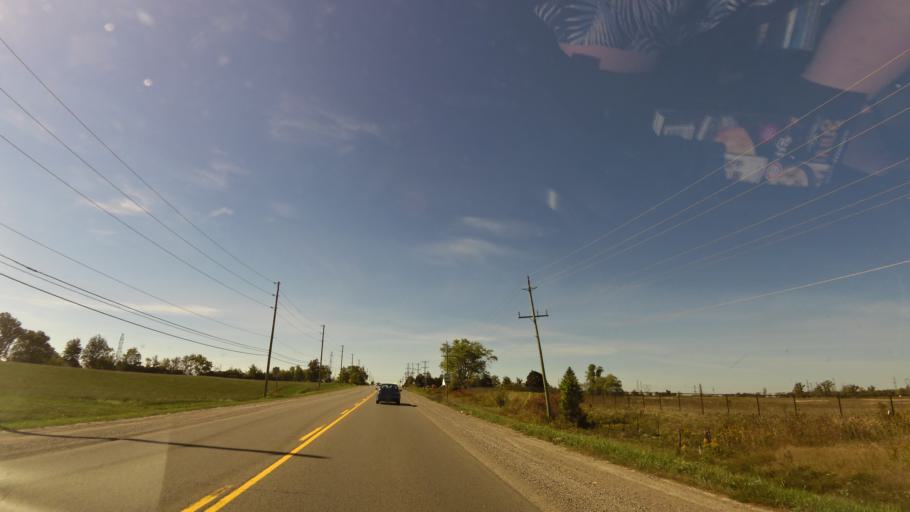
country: CA
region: Ontario
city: Ancaster
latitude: 43.0578
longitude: -79.9652
